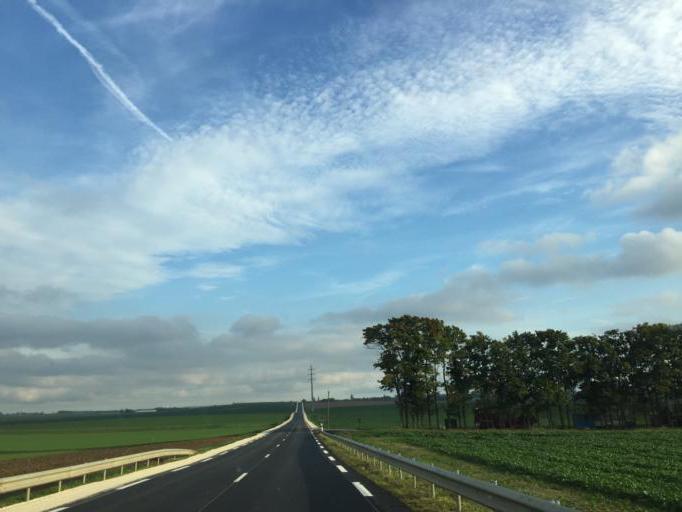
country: FR
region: Ile-de-France
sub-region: Departement de Seine-et-Marne
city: Touquin
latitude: 48.7022
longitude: 3.0627
